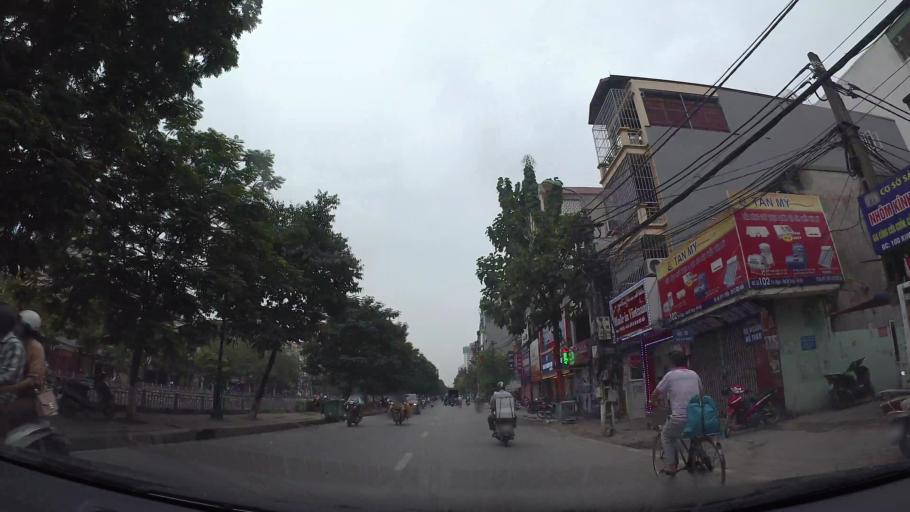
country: VN
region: Ha Noi
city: Hai BaTrung
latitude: 21.0051
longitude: 105.8611
